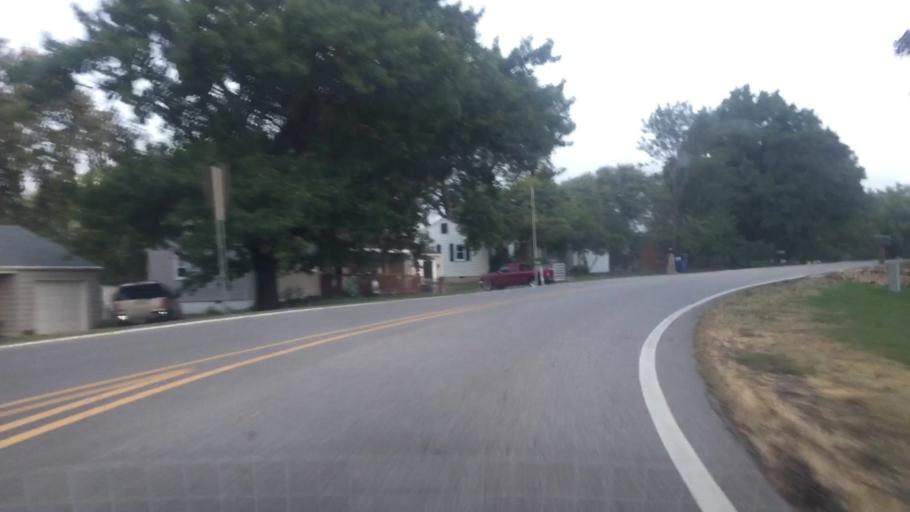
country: US
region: Kansas
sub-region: Johnson County
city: Shawnee
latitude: 39.0418
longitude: -94.7558
